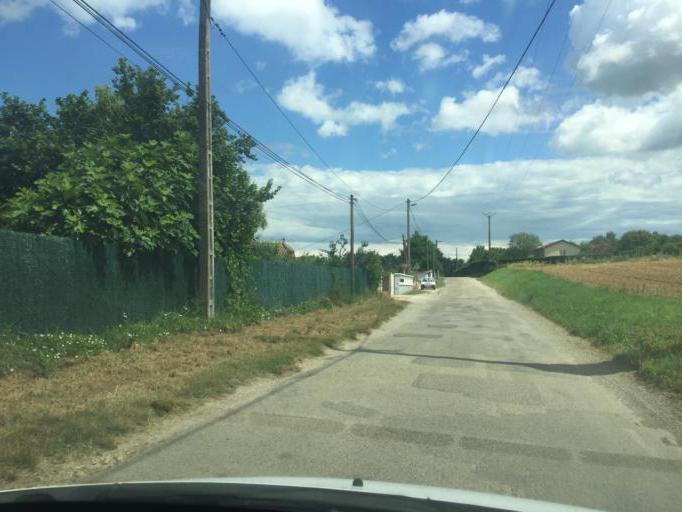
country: FR
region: Rhone-Alpes
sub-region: Departement de l'Isere
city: Charvieu-Chavagneux
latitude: 45.7561
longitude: 5.1569
